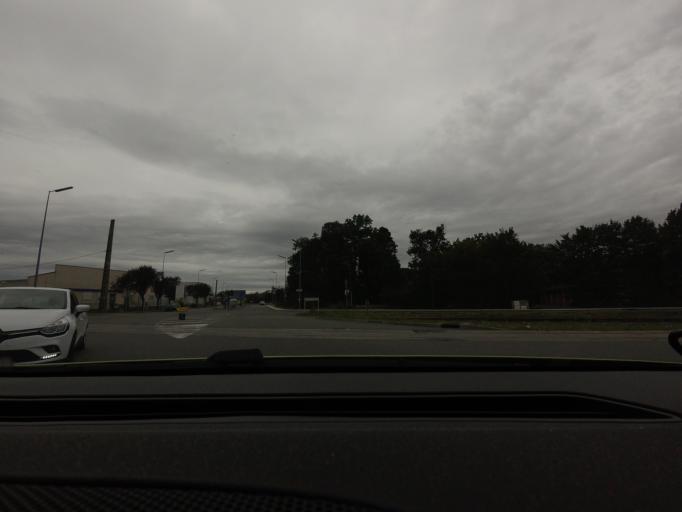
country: FR
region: Midi-Pyrenees
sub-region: Departement de la Haute-Garonne
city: Tournefeuille
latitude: 43.6041
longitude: 1.3137
